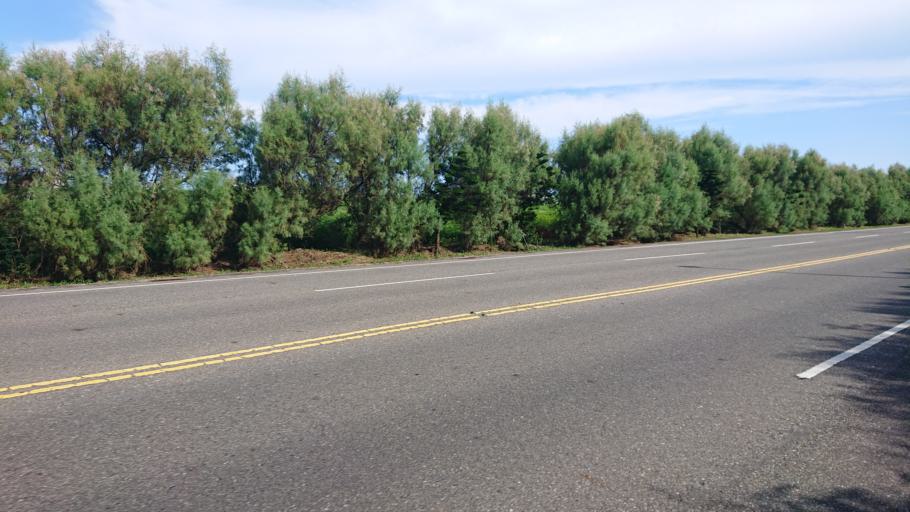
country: TW
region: Taiwan
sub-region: Penghu
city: Ma-kung
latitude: 23.5277
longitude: 119.5974
